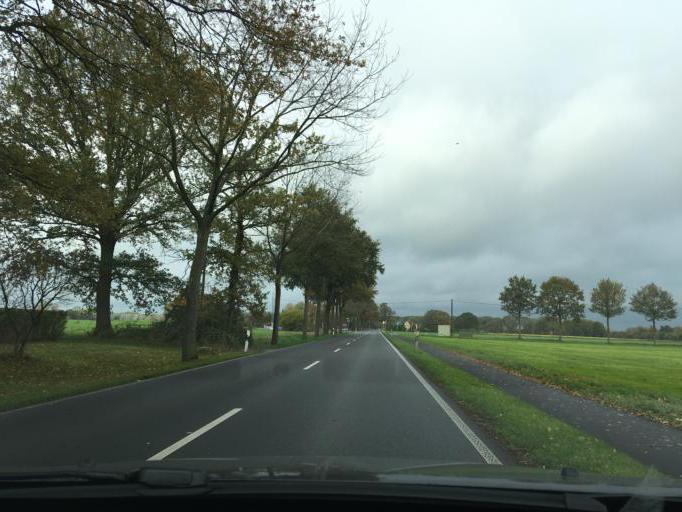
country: DE
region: North Rhine-Westphalia
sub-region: Regierungsbezirk Munster
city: Vreden
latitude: 52.0624
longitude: 6.7950
